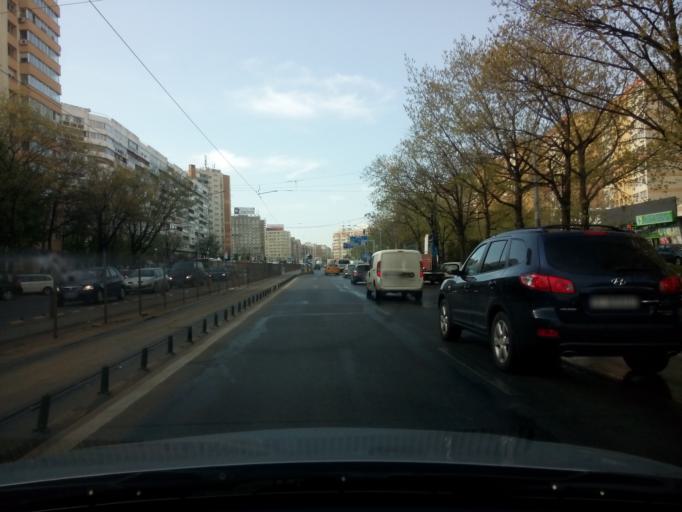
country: RO
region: Bucuresti
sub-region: Municipiul Bucuresti
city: Bucharest
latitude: 44.4525
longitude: 26.1268
